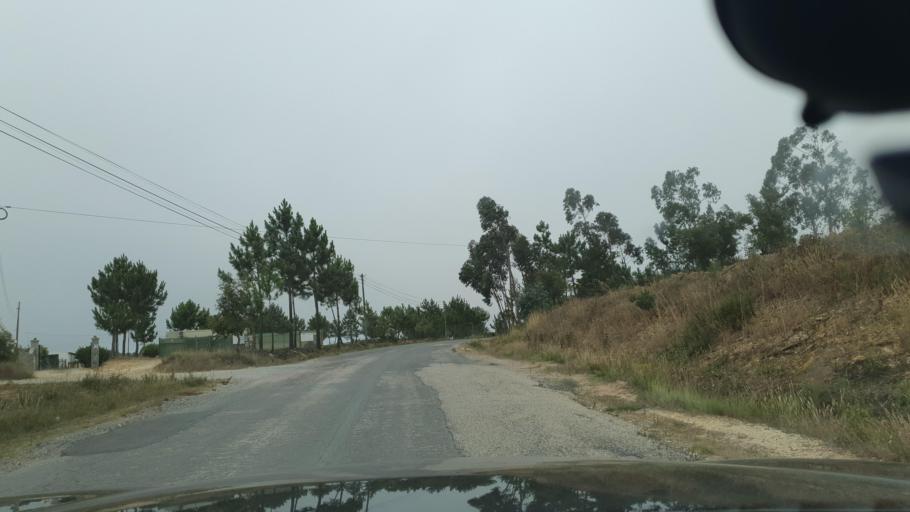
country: PT
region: Beja
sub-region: Odemira
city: Sao Teotonio
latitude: 37.5056
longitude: -8.6929
